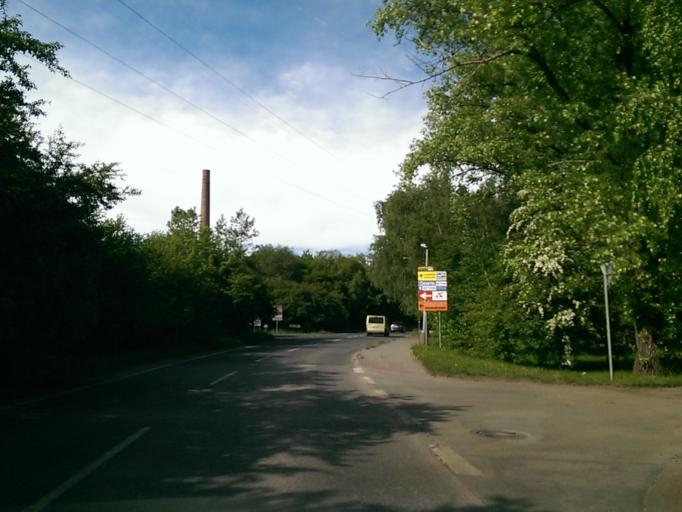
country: CZ
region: Praha
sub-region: Praha 20
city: Horni Pocernice
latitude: 50.0861
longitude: 14.6169
